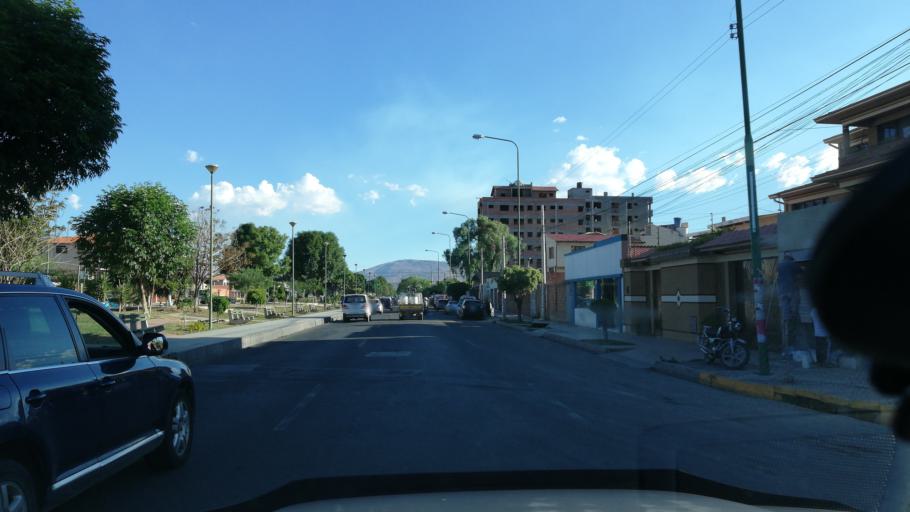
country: BO
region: Cochabamba
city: Cochabamba
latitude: -17.3852
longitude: -66.1822
